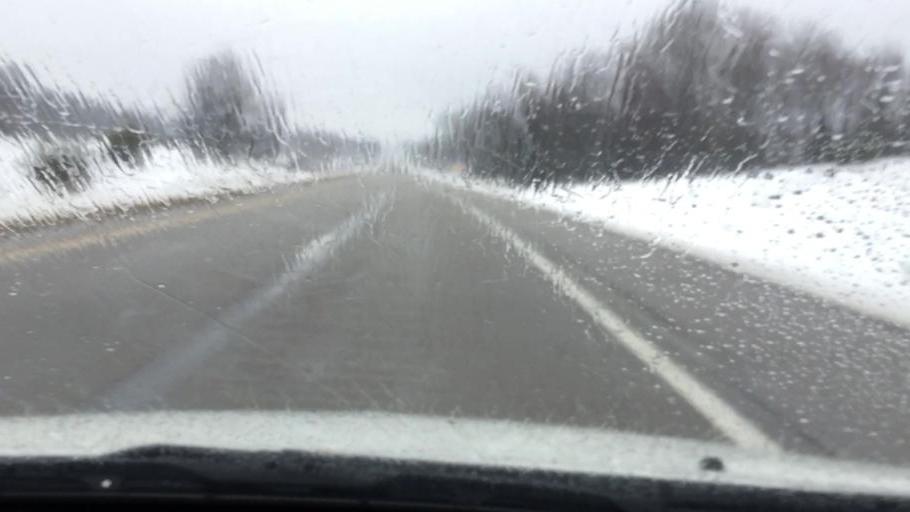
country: US
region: Michigan
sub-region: Wexford County
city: Cadillac
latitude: 44.1427
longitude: -85.4674
